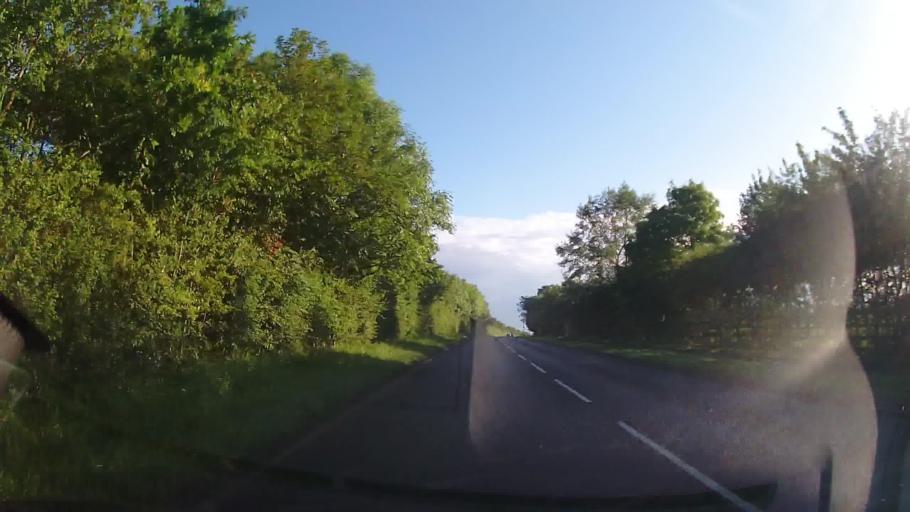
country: GB
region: England
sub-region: Leicestershire
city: Glenfield
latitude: 52.6570
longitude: -1.2155
